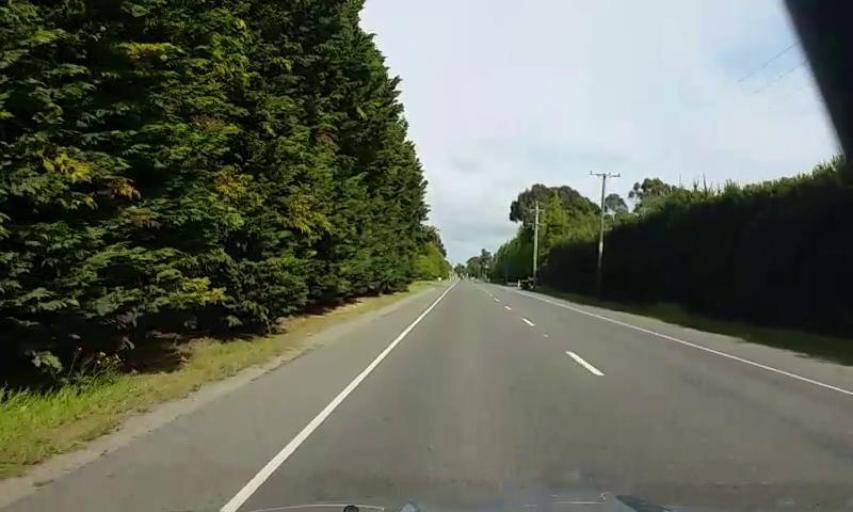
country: NZ
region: Canterbury
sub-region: Selwyn District
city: Prebbleton
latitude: -43.5150
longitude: 172.5166
